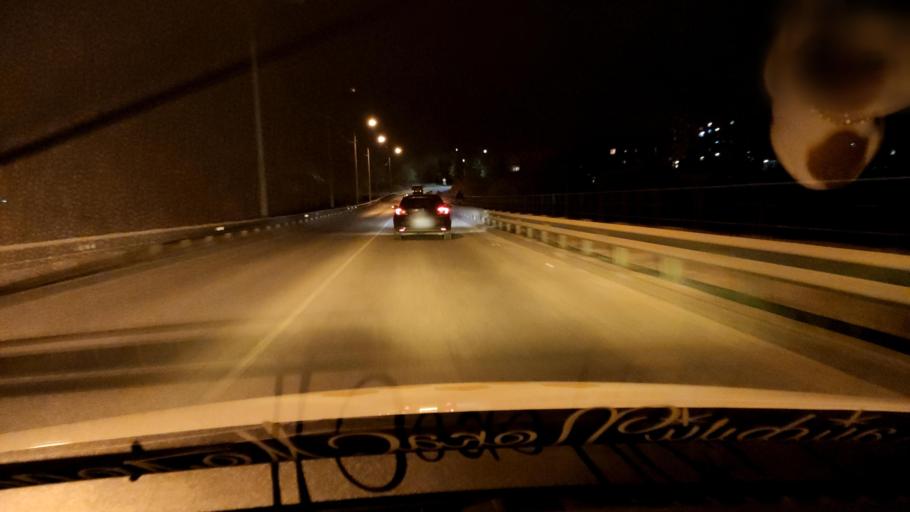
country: RU
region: Voronezj
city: Semiluki
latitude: 51.6759
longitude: 39.0315
